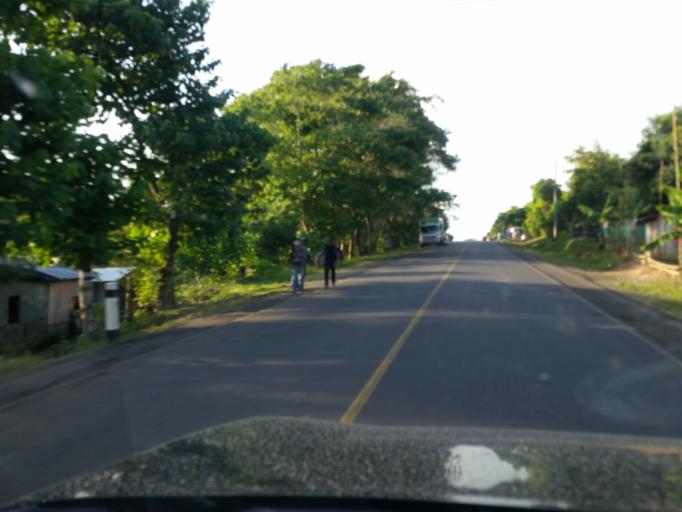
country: NI
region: Rio San Juan
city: San Carlos
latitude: 11.2820
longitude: -84.7176
